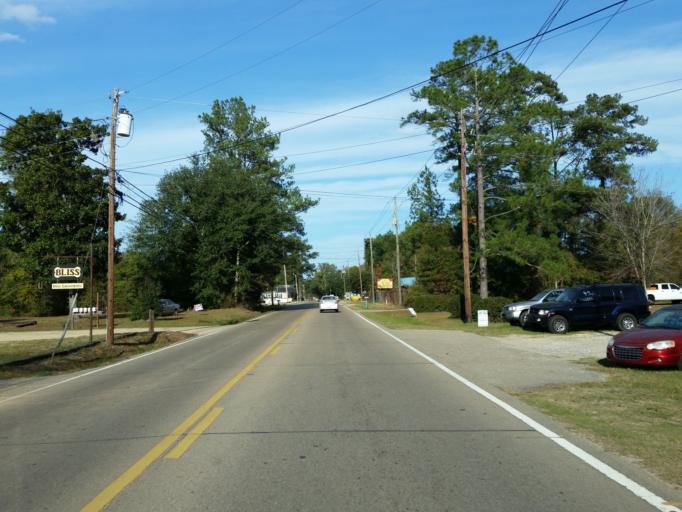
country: US
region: Mississippi
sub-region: Jones County
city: Ellisville
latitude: 31.6476
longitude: -89.1748
